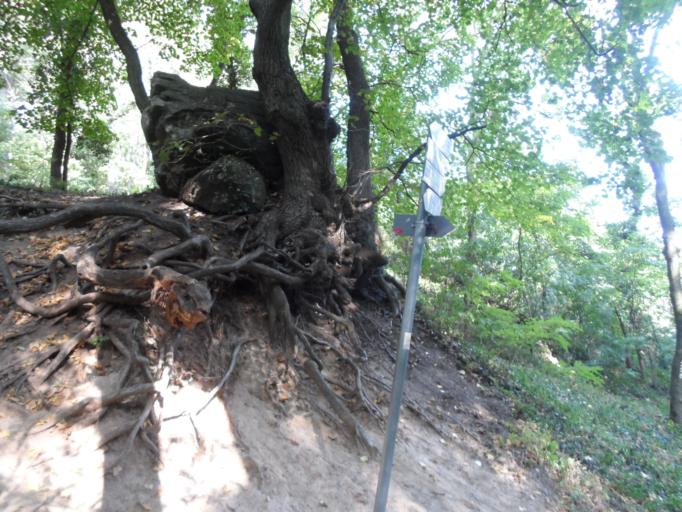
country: HU
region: Veszprem
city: Devecser
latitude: 47.1504
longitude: 17.3720
